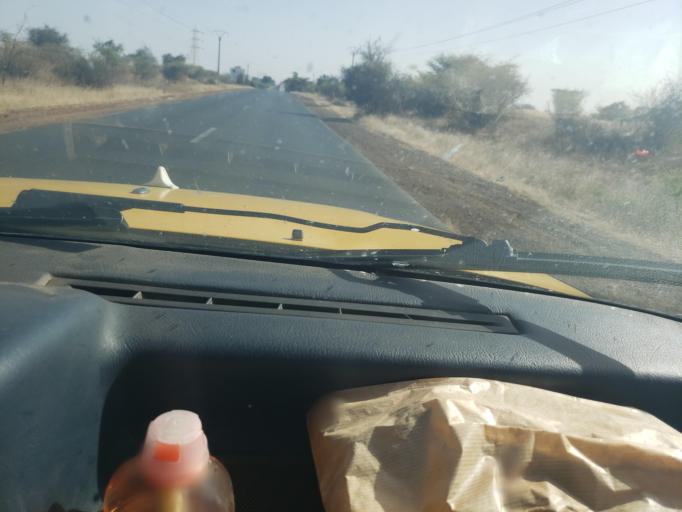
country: SN
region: Louga
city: Louga
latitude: 15.6575
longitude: -16.2571
